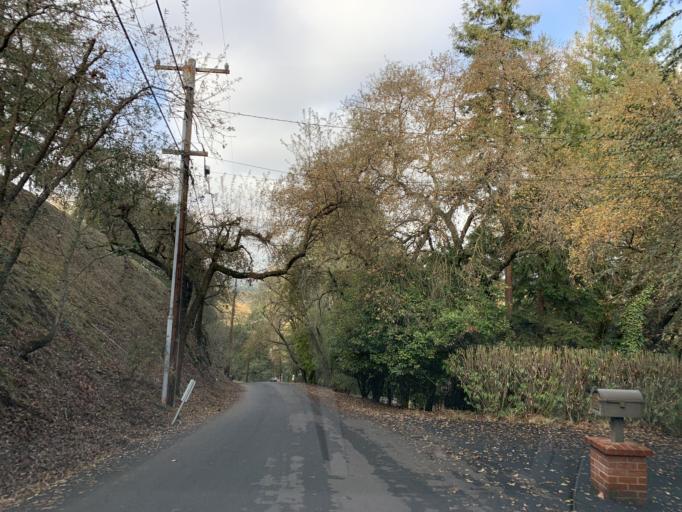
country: US
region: California
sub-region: Contra Costa County
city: Saranap
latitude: 37.8826
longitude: -122.0742
